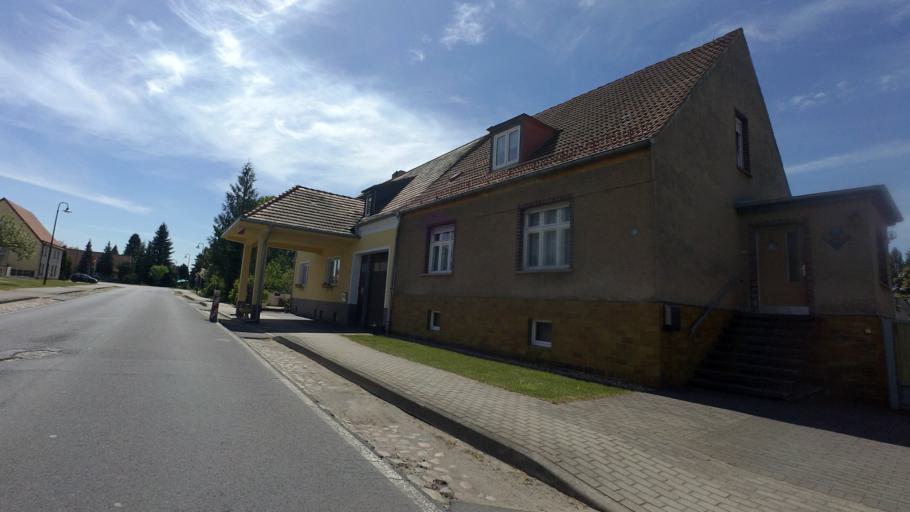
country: DE
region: Brandenburg
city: Luckenwalde
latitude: 52.0532
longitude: 13.2323
